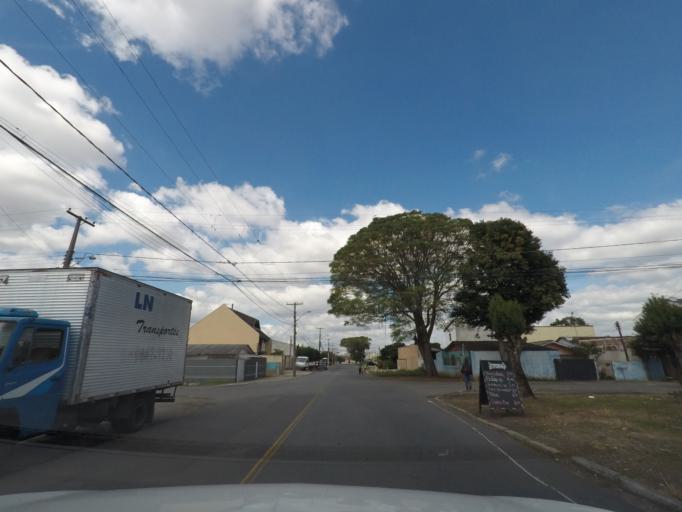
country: BR
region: Parana
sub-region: Sao Jose Dos Pinhais
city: Sao Jose dos Pinhais
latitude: -25.5068
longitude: -49.2194
